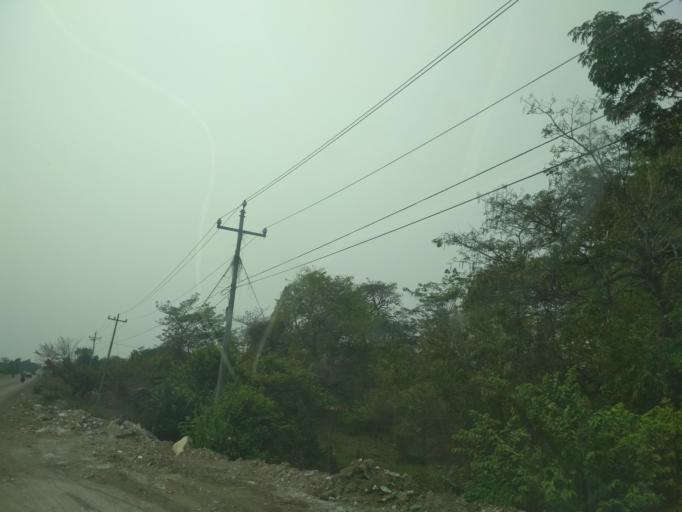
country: MX
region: Veracruz
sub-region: Veracruz
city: Delfino Victoria (Santa Fe)
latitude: 19.1948
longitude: -96.2904
